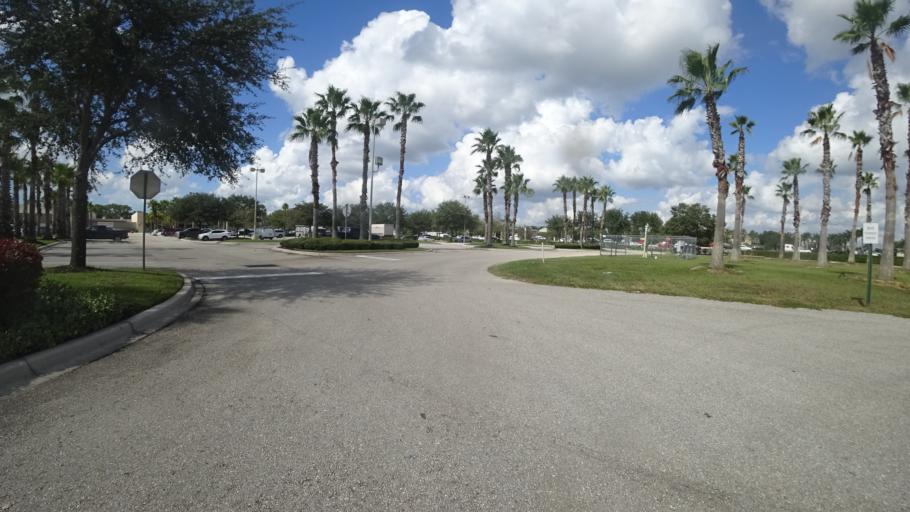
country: US
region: Florida
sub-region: Sarasota County
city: The Meadows
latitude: 27.3875
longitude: -82.4565
